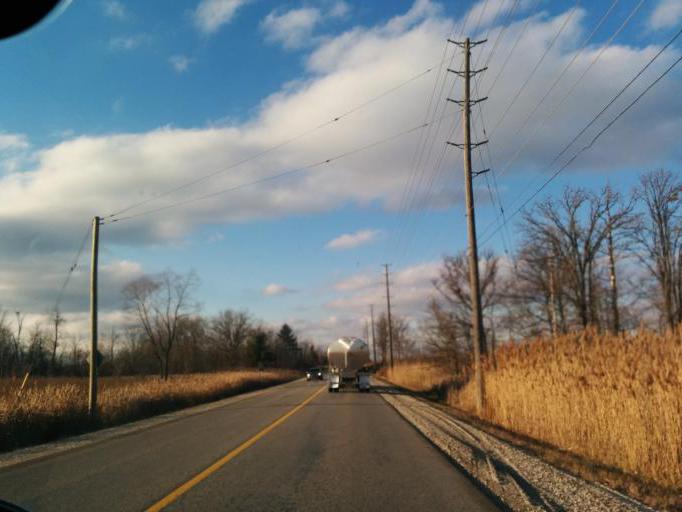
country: CA
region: Ontario
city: Oakville
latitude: 43.5171
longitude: -79.7094
